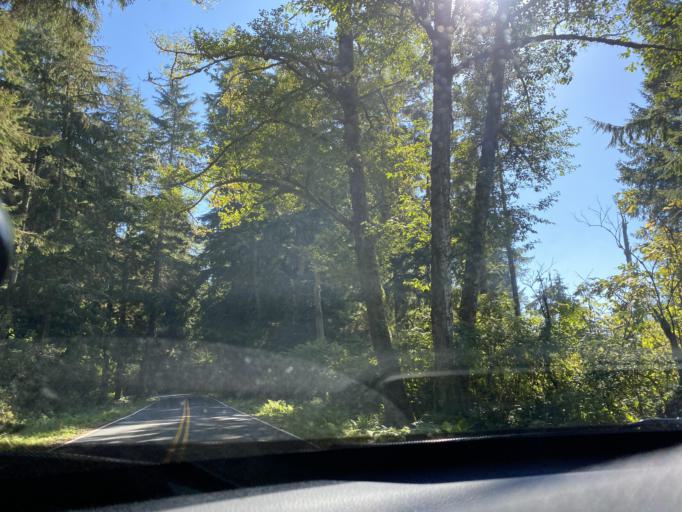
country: US
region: Washington
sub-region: Clallam County
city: Forks
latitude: 47.9204
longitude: -124.6124
